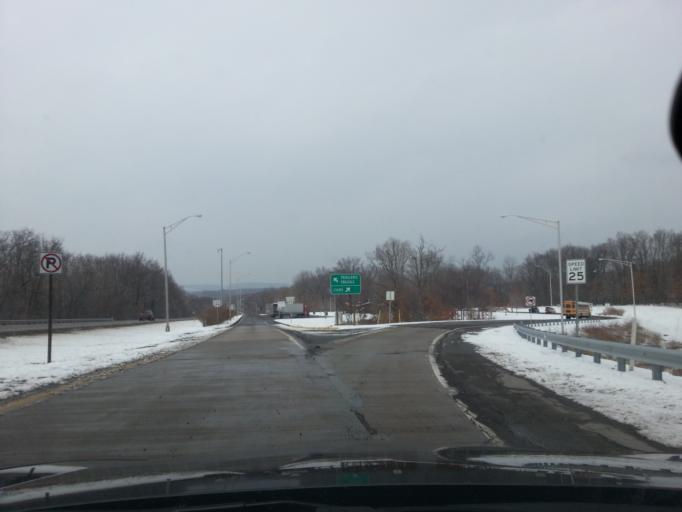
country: US
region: Pennsylvania
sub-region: Luzerne County
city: Freeland
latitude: 41.1001
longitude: -75.9609
